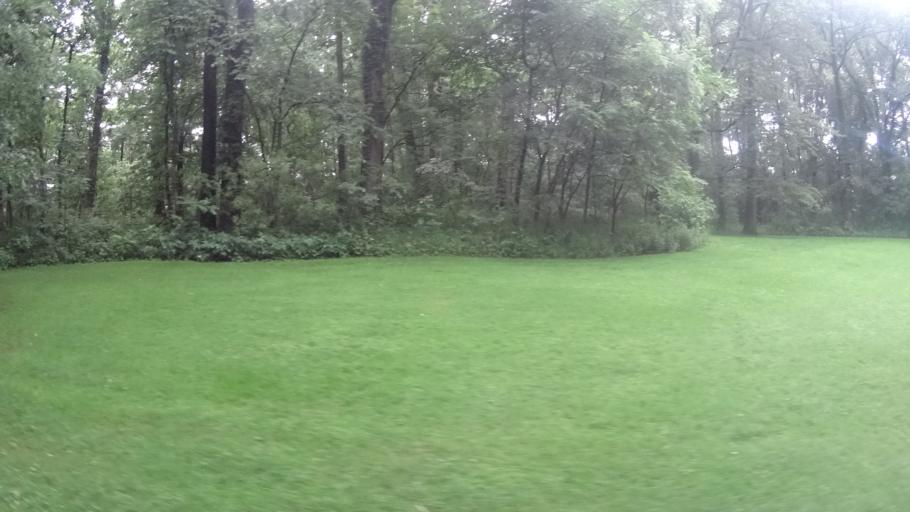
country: US
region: Ohio
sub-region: Erie County
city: Huron
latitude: 41.3568
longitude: -82.5834
